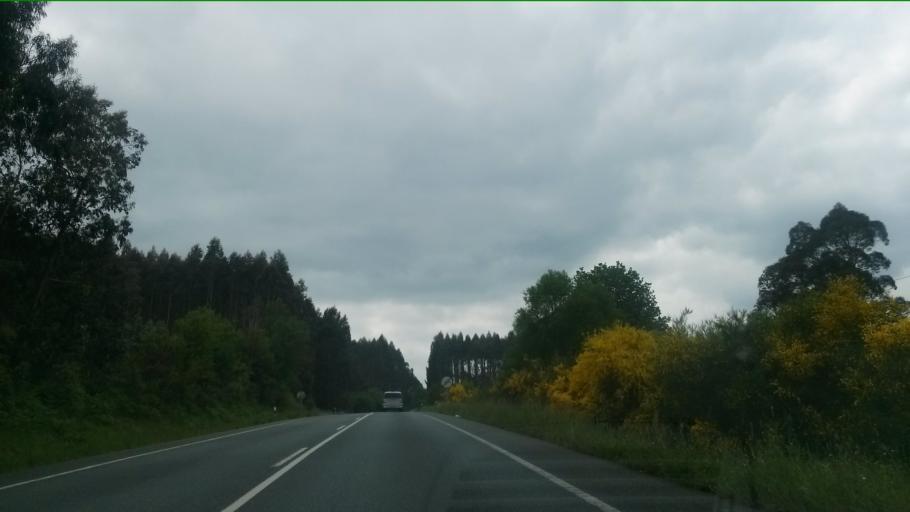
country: ES
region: Galicia
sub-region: Provincia da Coruna
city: Curtis
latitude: 43.1234
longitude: -8.0684
